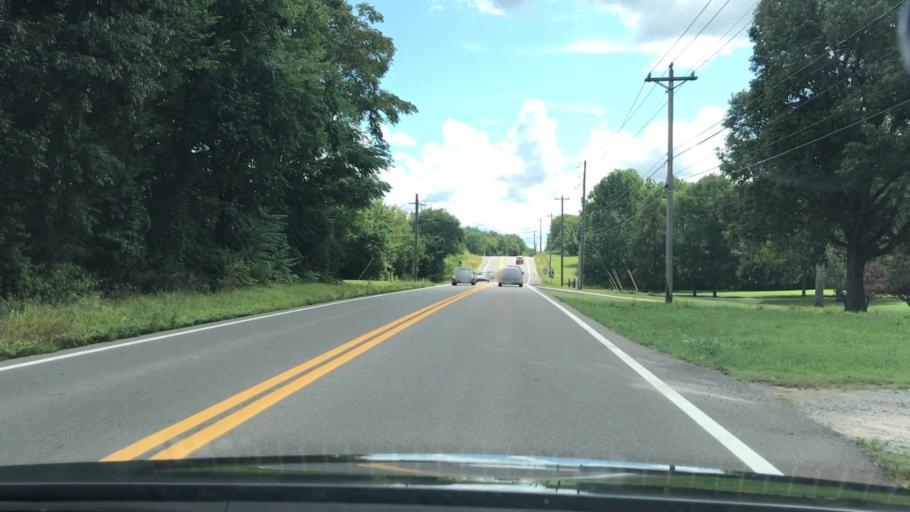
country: US
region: Tennessee
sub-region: Williamson County
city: Nolensville
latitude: 35.8508
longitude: -86.5888
